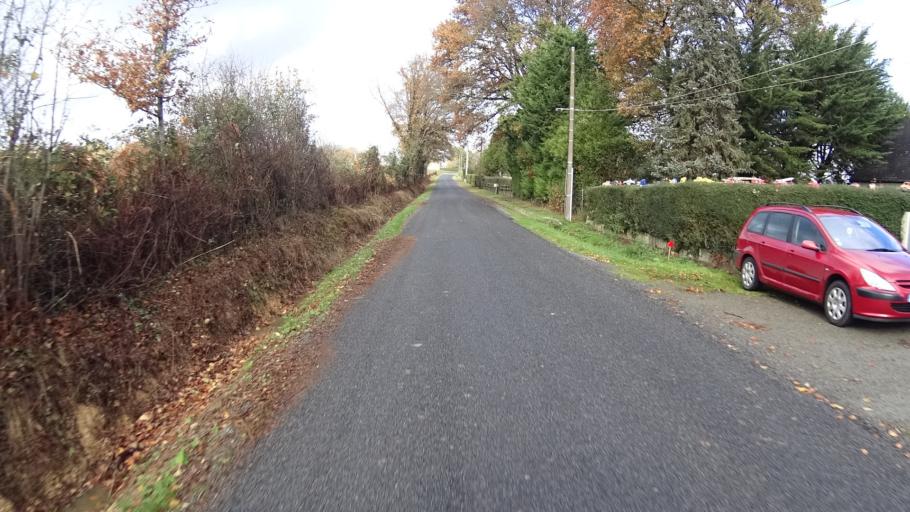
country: FR
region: Pays de la Loire
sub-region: Departement de la Loire-Atlantique
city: Fegreac
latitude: 47.6074
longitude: -2.0669
